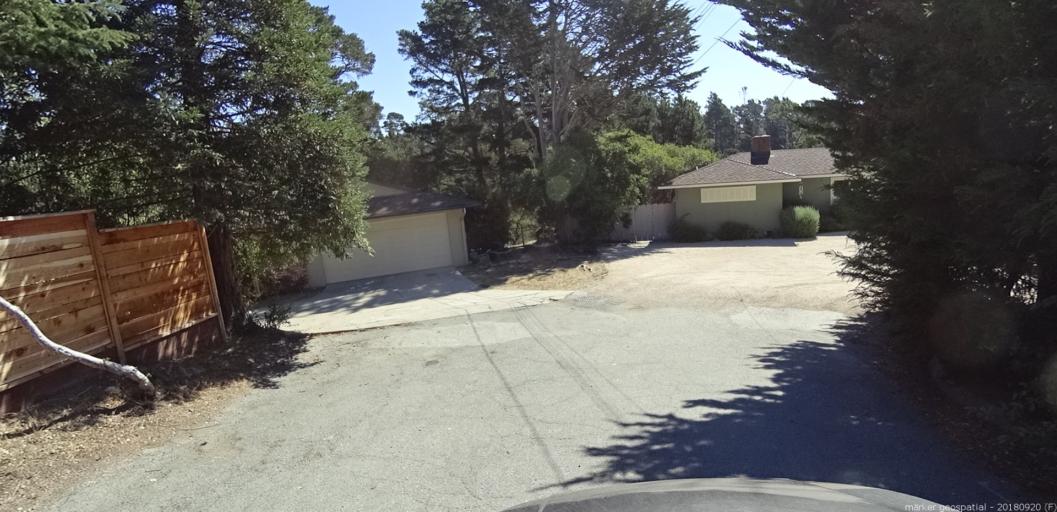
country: US
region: California
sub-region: Monterey County
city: Carmel-by-the-Sea
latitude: 36.5517
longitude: -121.9080
